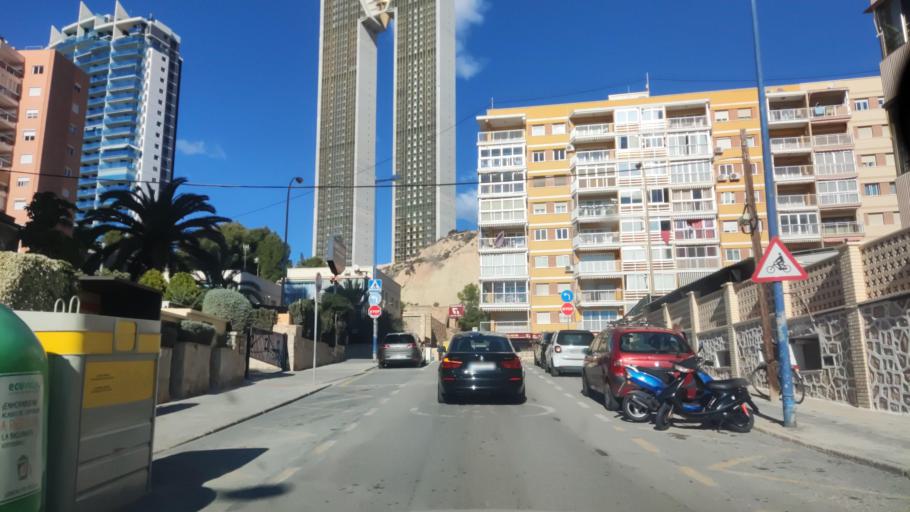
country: ES
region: Valencia
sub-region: Provincia de Alicante
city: Benidorm
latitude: 38.5356
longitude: -0.1528
